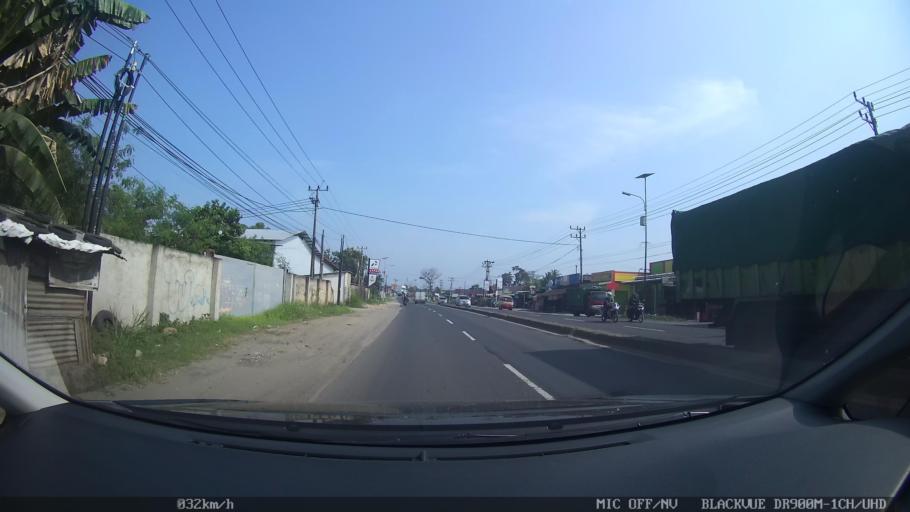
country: ID
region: Lampung
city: Natar
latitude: -5.2642
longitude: 105.1854
